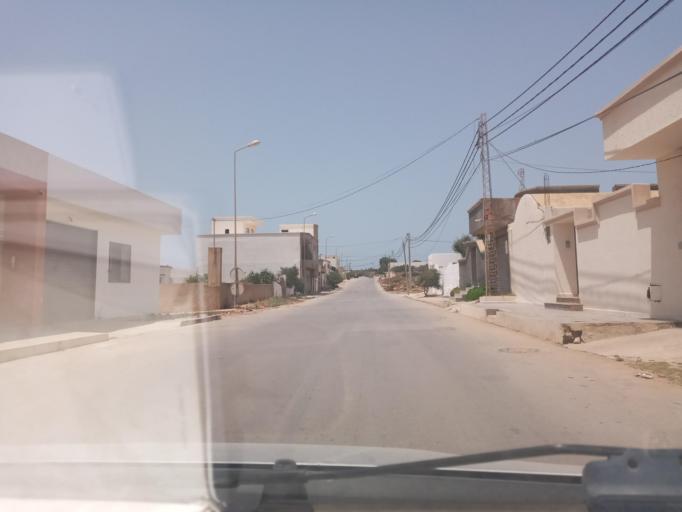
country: TN
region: Nabul
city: El Haouaria
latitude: 37.0544
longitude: 11.0053
